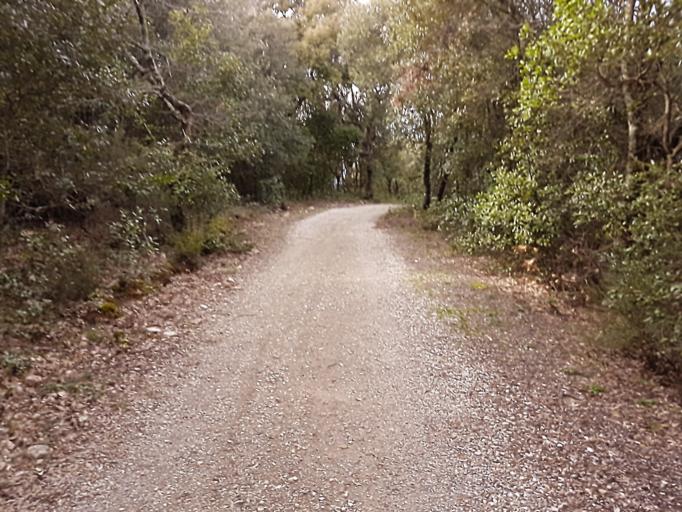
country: IT
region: Umbria
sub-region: Provincia di Perugia
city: Corciano
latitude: 43.1330
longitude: 12.3012
